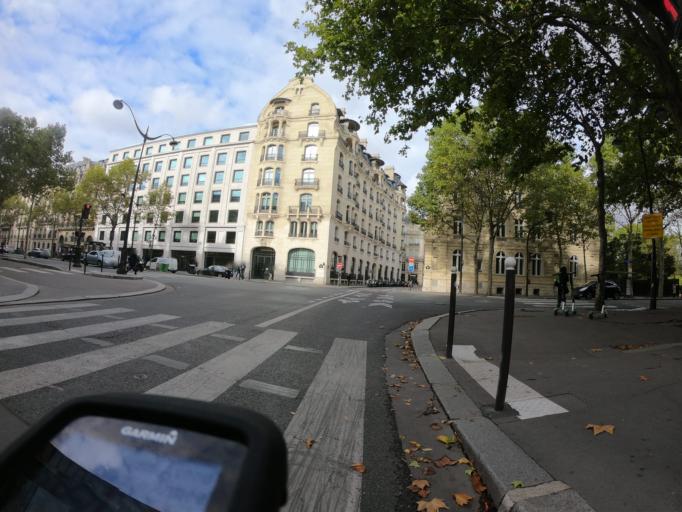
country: FR
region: Ile-de-France
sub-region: Departement des Hauts-de-Seine
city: Levallois-Perret
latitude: 48.8724
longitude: 2.2943
